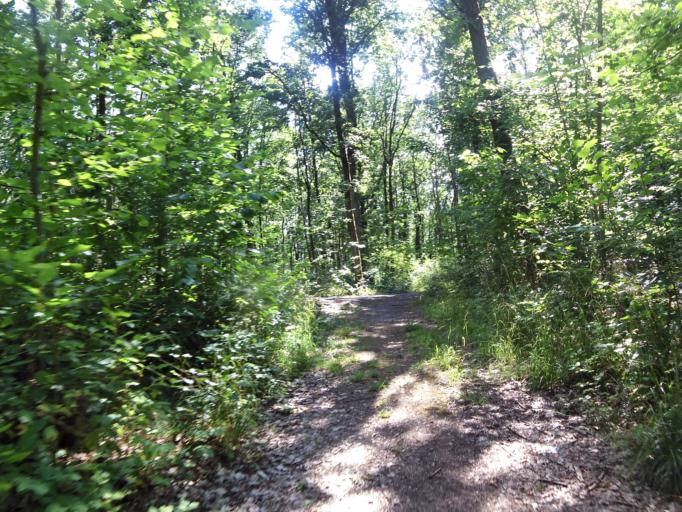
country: DE
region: Bavaria
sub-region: Regierungsbezirk Unterfranken
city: Rimpar
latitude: 49.8381
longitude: 9.9706
